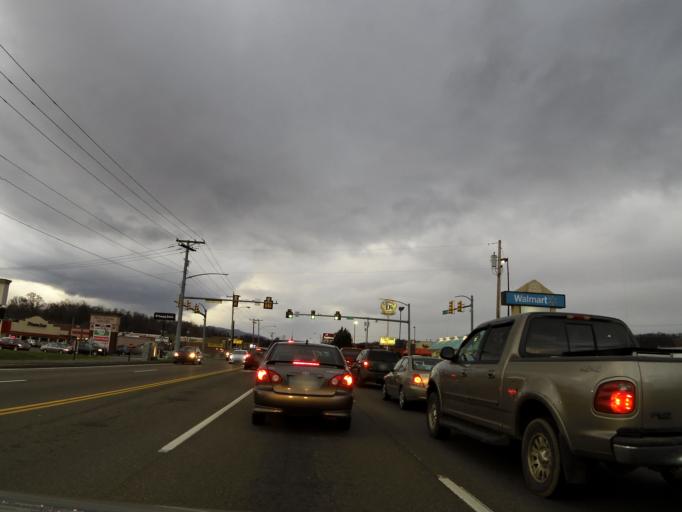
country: US
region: Tennessee
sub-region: Carter County
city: Elizabethton
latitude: 36.3475
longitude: -82.2435
